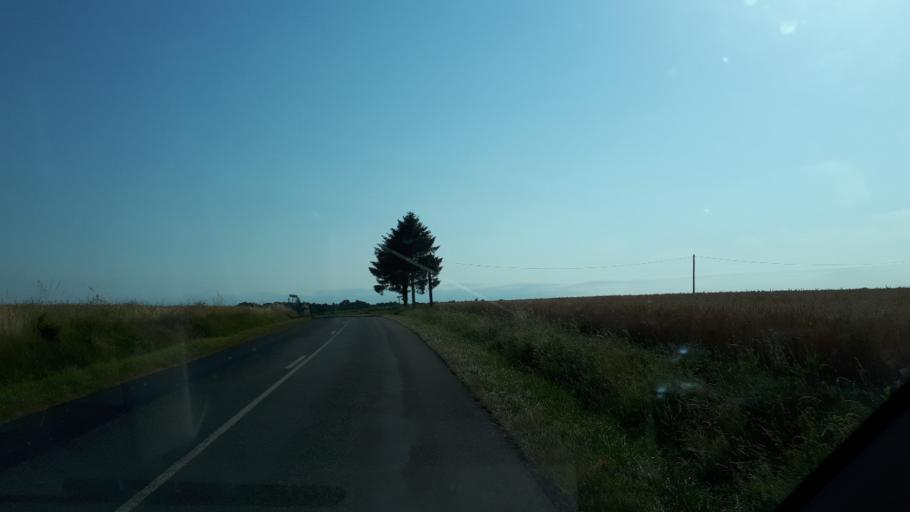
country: FR
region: Centre
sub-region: Departement du Loir-et-Cher
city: Aze
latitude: 47.8781
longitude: 1.0112
